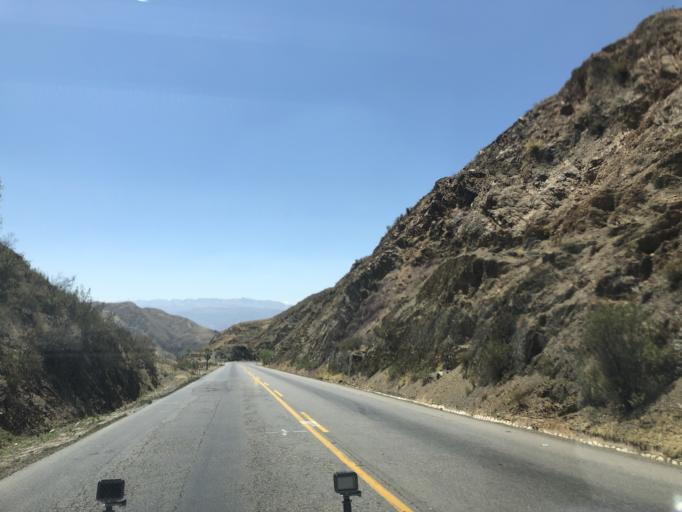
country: BO
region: Cochabamba
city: Irpa Irpa
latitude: -17.6759
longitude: -66.4238
